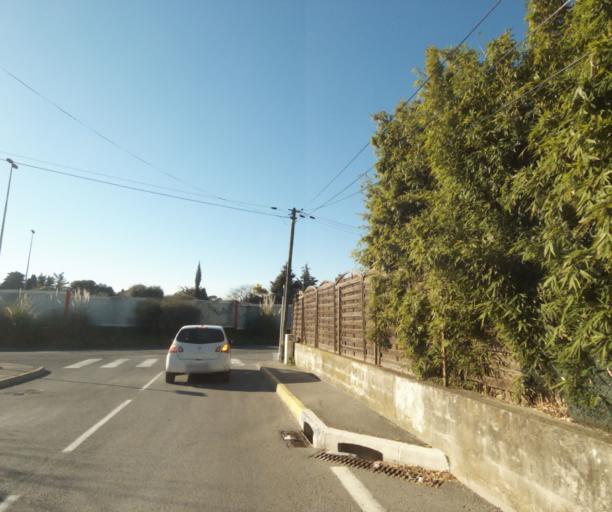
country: FR
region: Provence-Alpes-Cote d'Azur
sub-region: Departement des Alpes-Maritimes
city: Antibes
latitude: 43.5798
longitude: 7.0942
